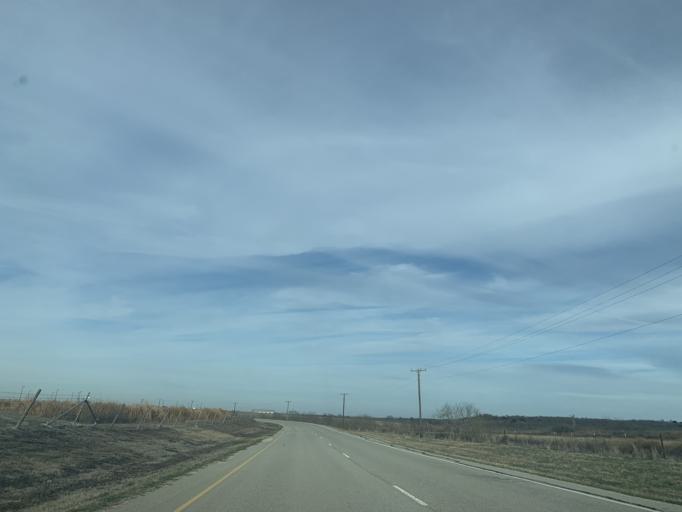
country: US
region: Texas
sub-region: Bell County
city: Salado
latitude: 30.9019
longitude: -97.5577
